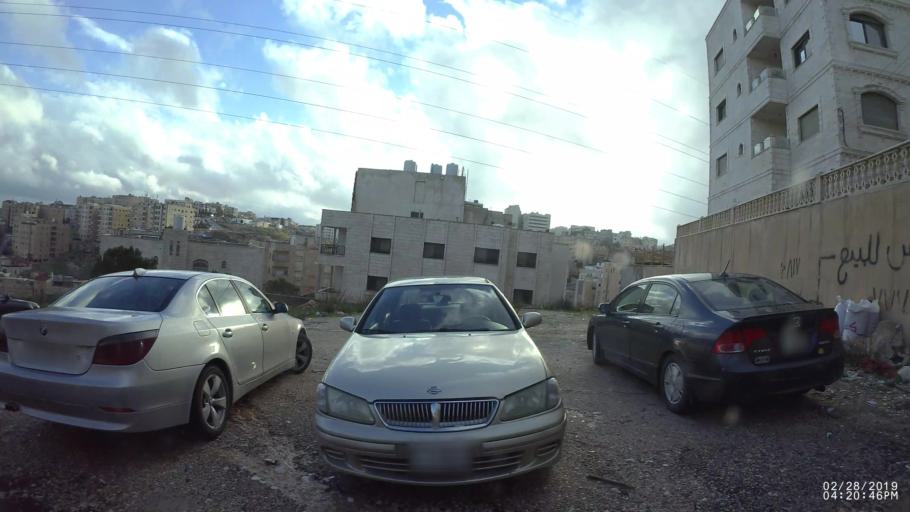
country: JO
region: Amman
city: Amman
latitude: 32.0035
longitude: 35.9243
